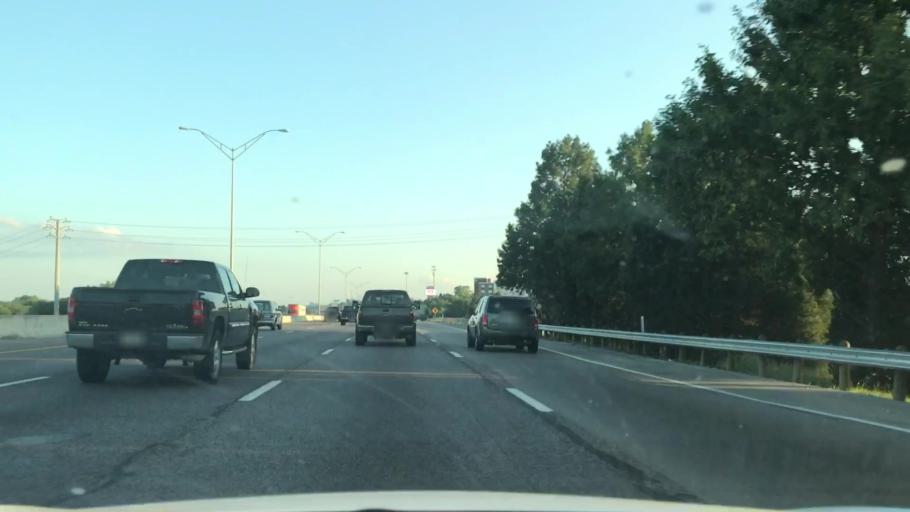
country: US
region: Texas
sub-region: Dallas County
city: Mesquite
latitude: 32.7686
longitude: -96.6225
